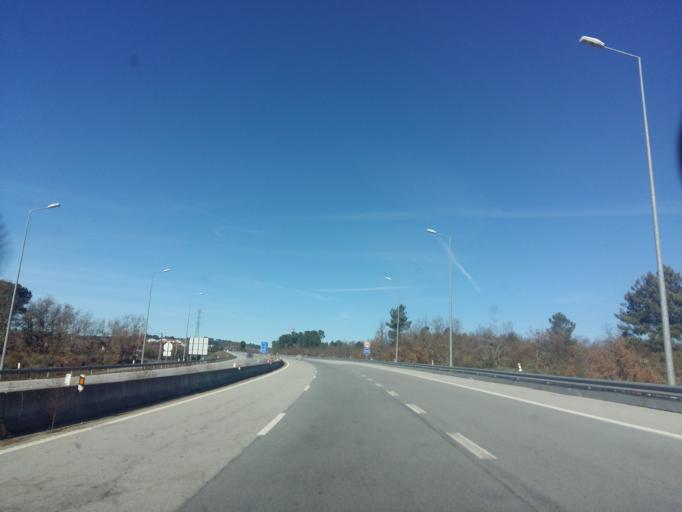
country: PT
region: Guarda
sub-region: Guarda
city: Sequeira
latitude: 40.5461
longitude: -7.2157
